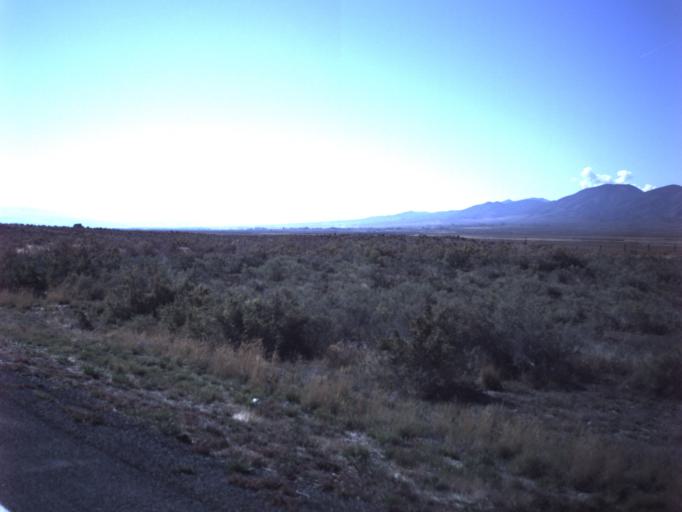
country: US
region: Utah
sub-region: Sanpete County
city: Gunnison
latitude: 39.2911
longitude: -111.8870
